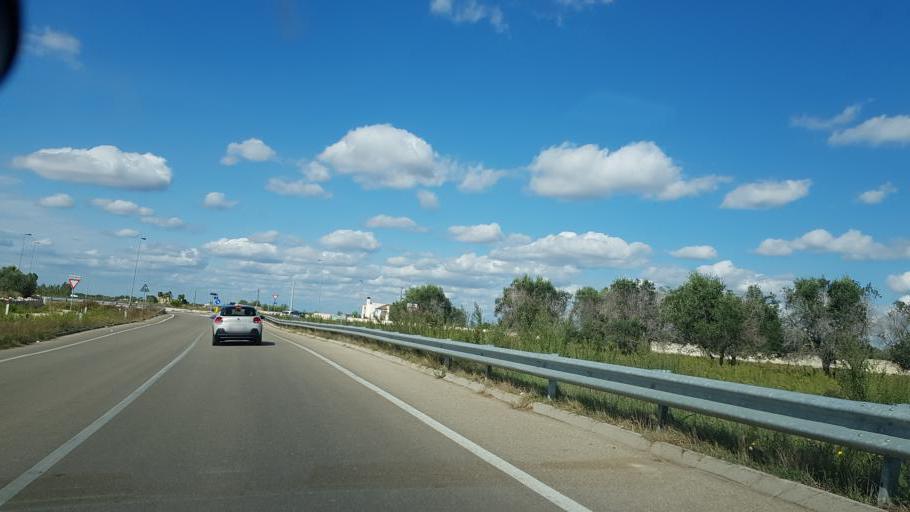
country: IT
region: Apulia
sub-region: Provincia di Lecce
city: Leverano
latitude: 40.3039
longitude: 18.0077
